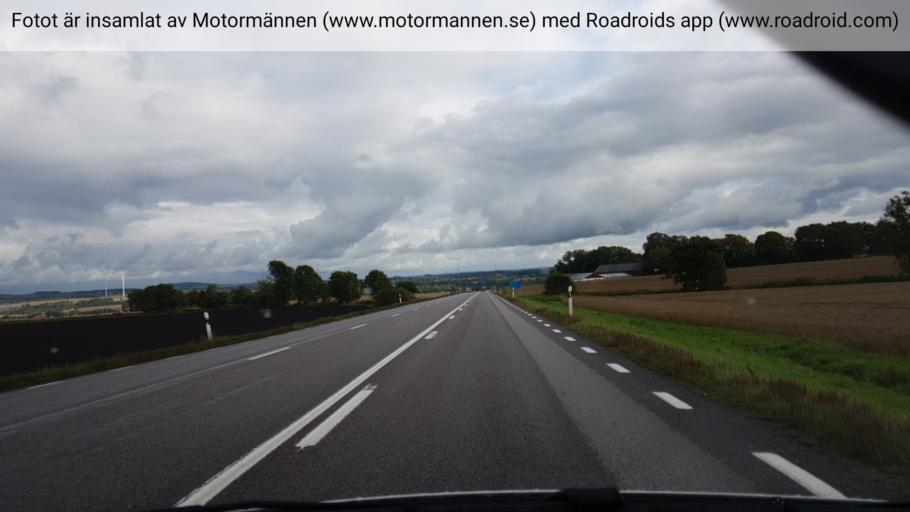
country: SE
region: Vaestra Goetaland
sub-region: Falkopings Kommun
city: Falkoeping
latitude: 58.1430
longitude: 13.6278
